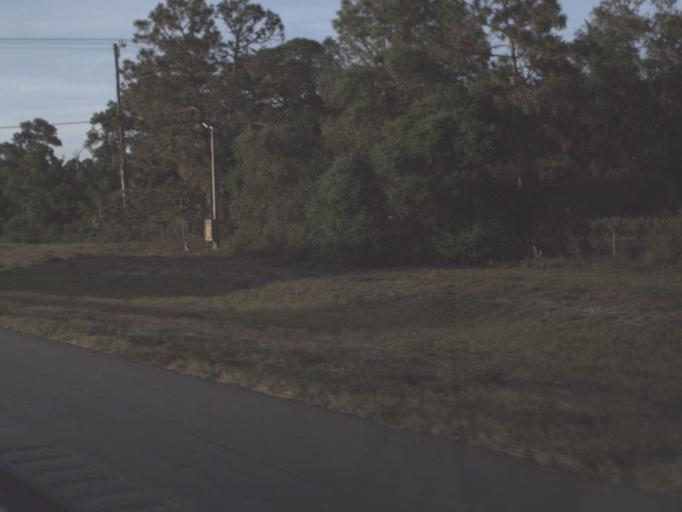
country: US
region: Florida
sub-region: Brevard County
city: Mims
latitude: 28.7148
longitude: -80.8895
